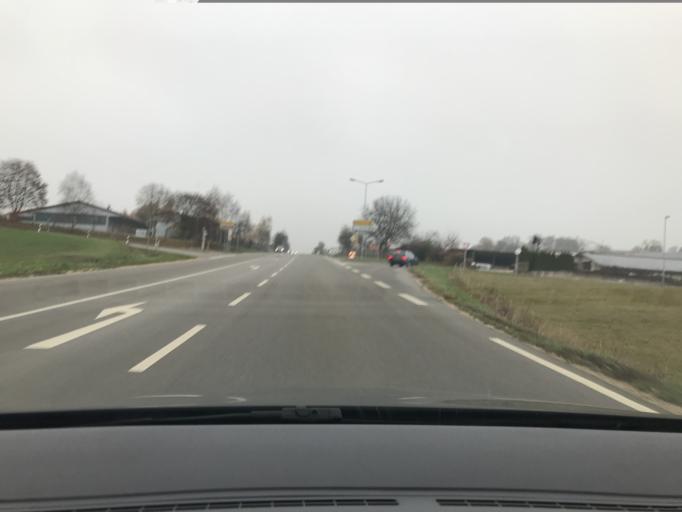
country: DE
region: Bavaria
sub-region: Swabia
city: Marktoffingen
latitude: 48.9230
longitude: 10.4656
